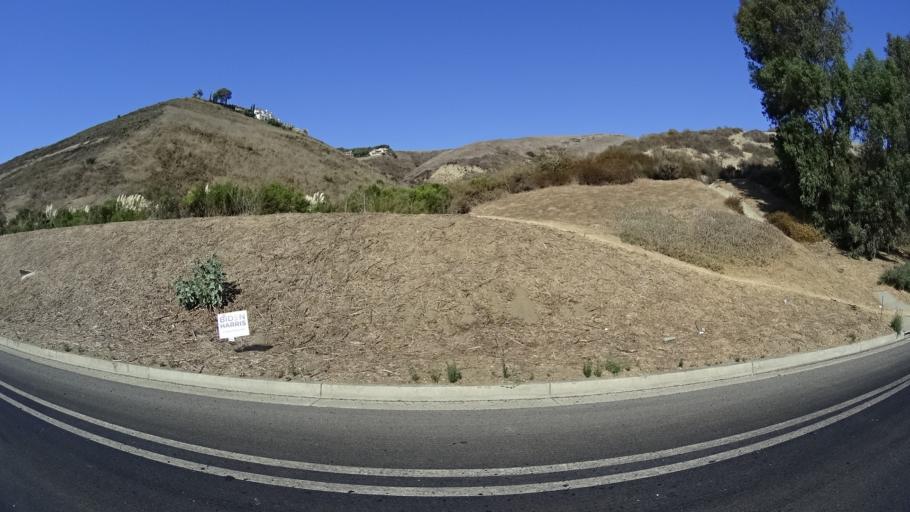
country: US
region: California
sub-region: Orange County
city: San Juan Capistrano
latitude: 33.4653
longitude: -117.6401
